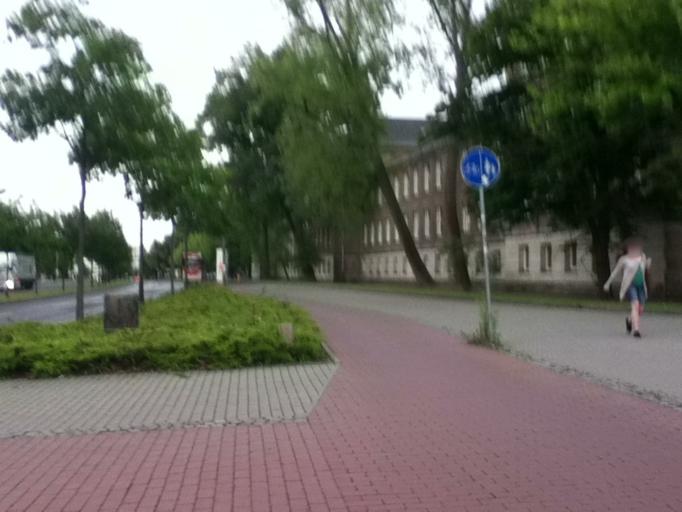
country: DE
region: Saxony
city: Dresden
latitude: 51.0294
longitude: 13.7324
